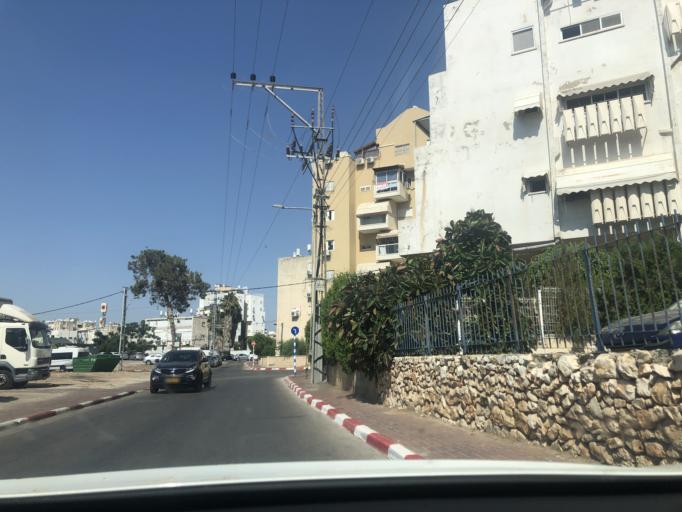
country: IL
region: Central District
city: Lod
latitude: 31.9502
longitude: 34.8924
